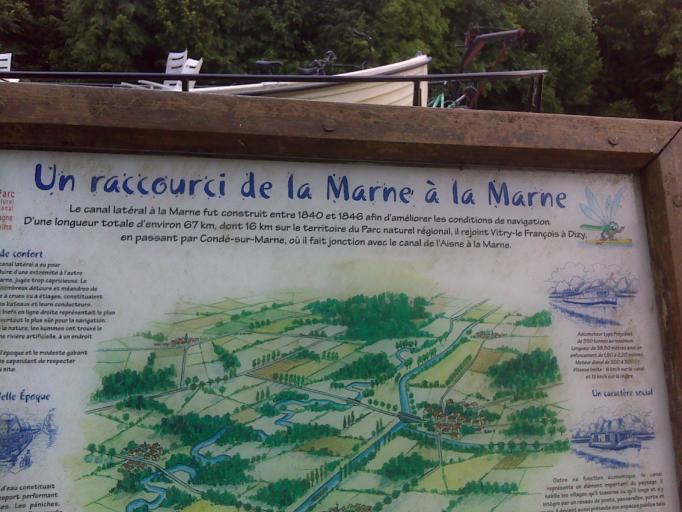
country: FR
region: Champagne-Ardenne
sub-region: Departement de la Marne
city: Mareuil-sur-Ay
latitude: 49.0446
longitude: 4.0360
